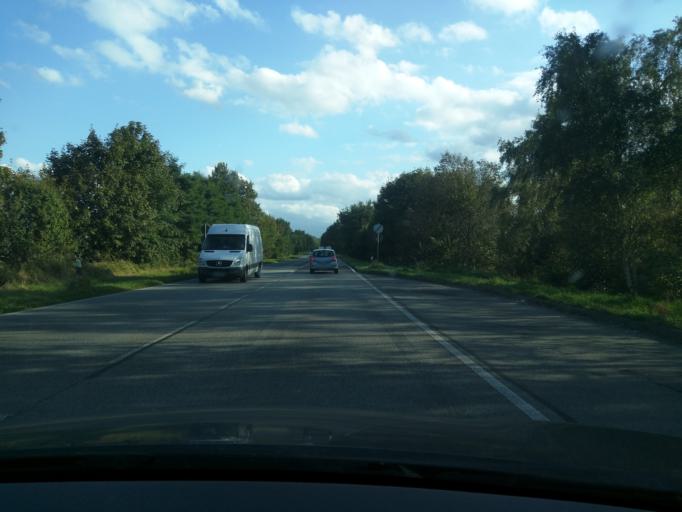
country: DE
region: Schleswig-Holstein
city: Escheburg
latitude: 53.4540
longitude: 10.3328
